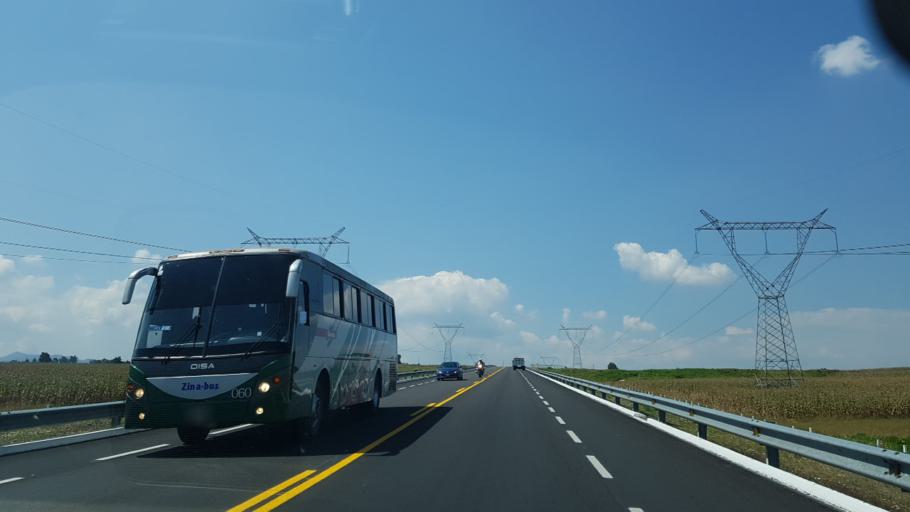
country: MX
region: Mexico
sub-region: Almoloya de Juarez
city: San Pedro de la Hortaliza (Ejido Almoloyan)
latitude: 19.3783
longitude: -99.8399
